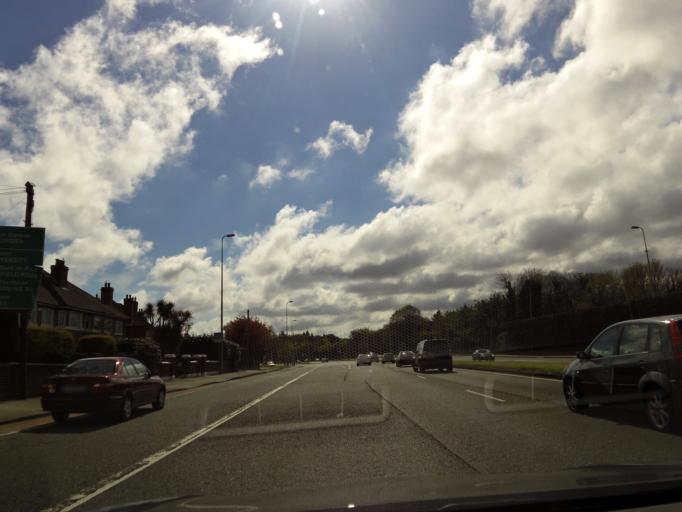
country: IE
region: Leinster
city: Donnybrook
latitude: 53.3120
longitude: -6.2205
